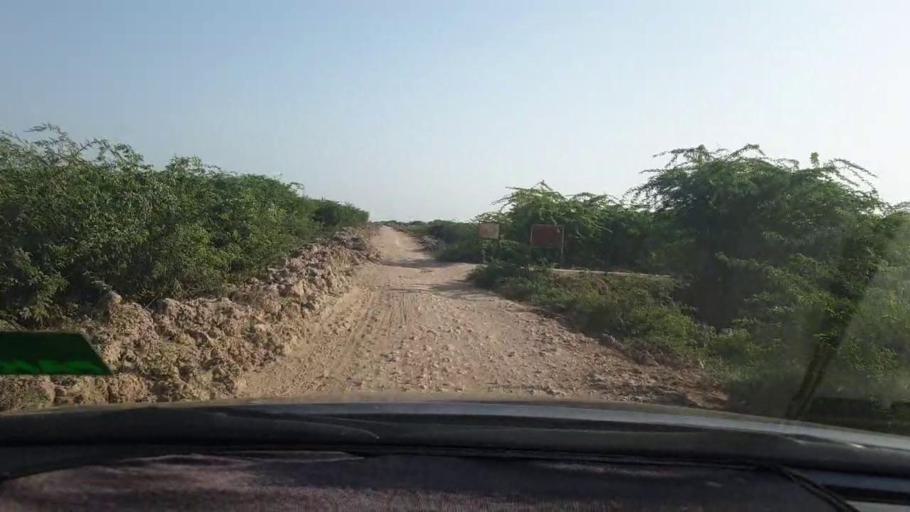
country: PK
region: Sindh
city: Naukot
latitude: 24.9111
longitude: 69.2766
